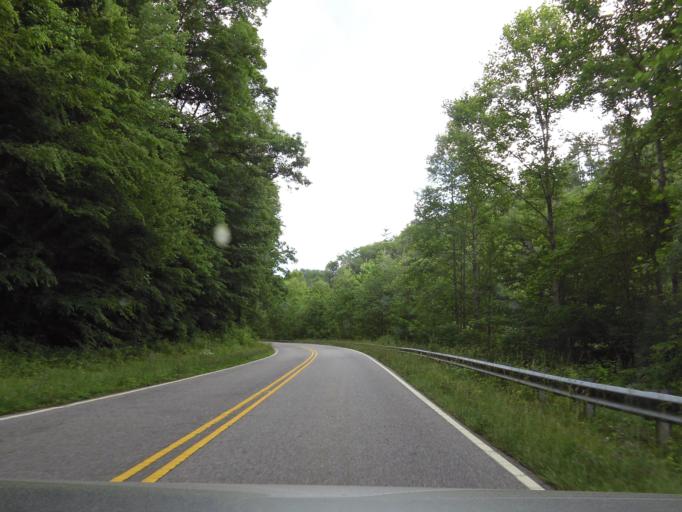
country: US
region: North Carolina
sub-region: Graham County
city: Robbinsville
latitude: 35.4005
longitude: -83.8804
